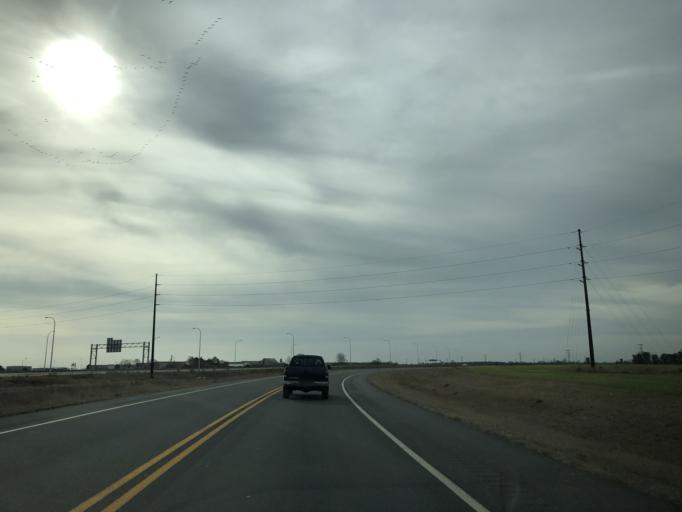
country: US
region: Delaware
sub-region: New Castle County
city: Middletown
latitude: 39.4435
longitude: -75.7552
